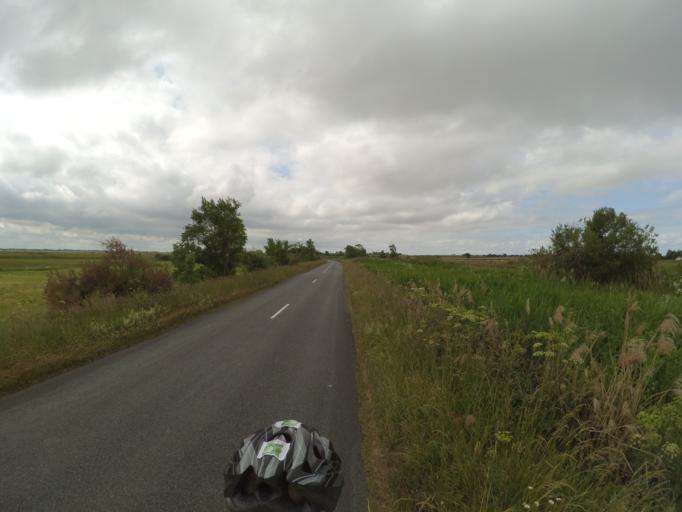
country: FR
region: Poitou-Charentes
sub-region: Departement de la Charente-Maritime
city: Yves
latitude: 46.0323
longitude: -1.0475
